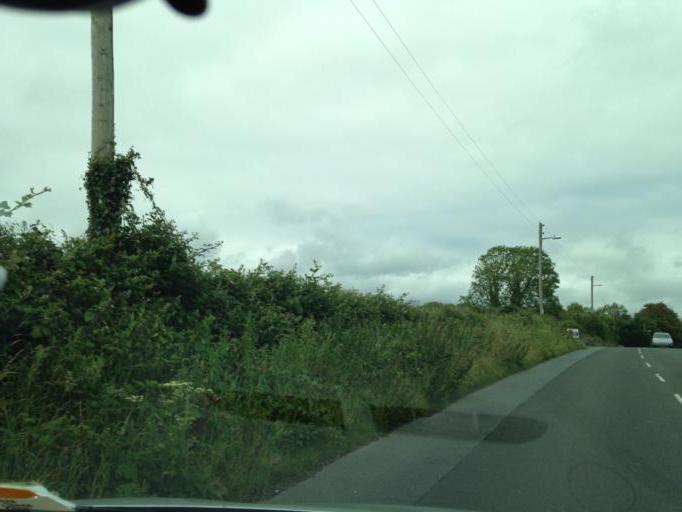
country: IE
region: Connaught
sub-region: County Galway
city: Gaillimh
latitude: 53.2860
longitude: -9.0564
